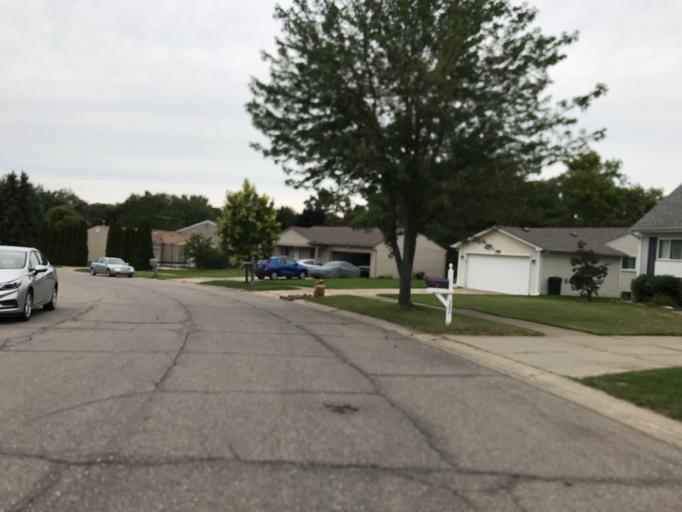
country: US
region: Michigan
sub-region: Oakland County
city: South Lyon
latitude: 42.4649
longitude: -83.6402
